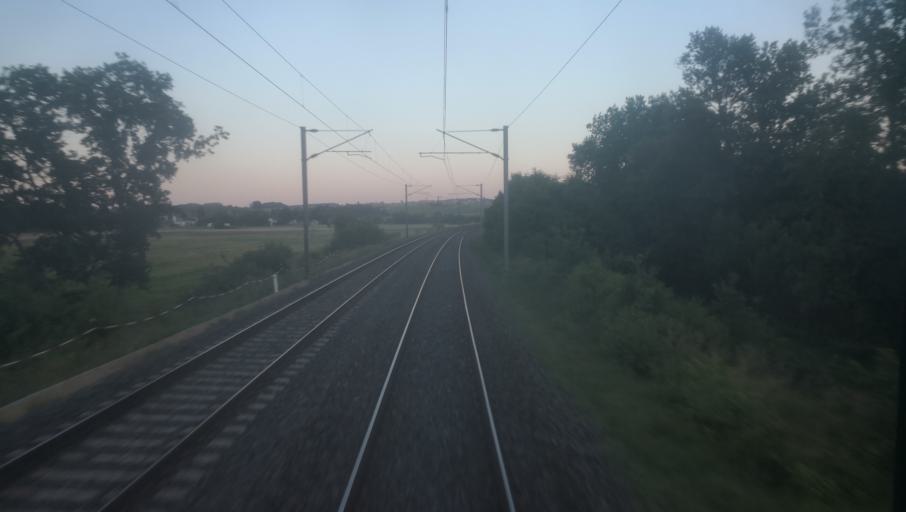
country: FR
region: Centre
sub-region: Departement du Cher
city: Saint-Satur
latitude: 47.3174
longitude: 2.8985
